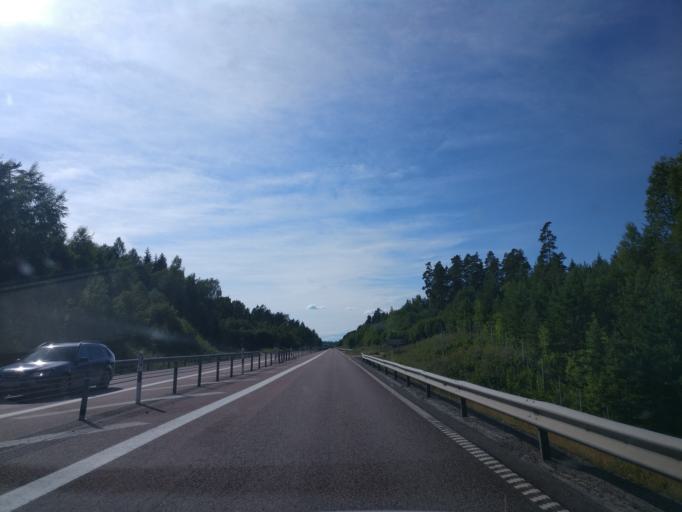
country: SE
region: Vaermland
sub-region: Kils Kommun
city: Kil
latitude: 59.4933
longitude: 13.3141
